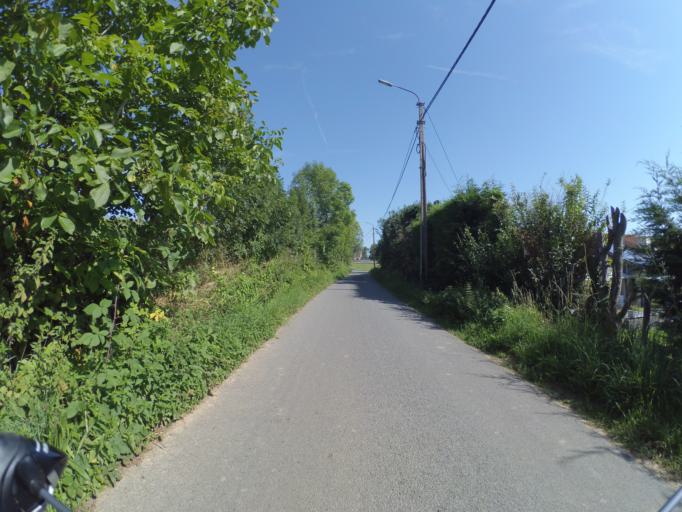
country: BE
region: Flanders
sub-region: Provincie Oost-Vlaanderen
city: Ronse
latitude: 50.7629
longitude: 3.6131
